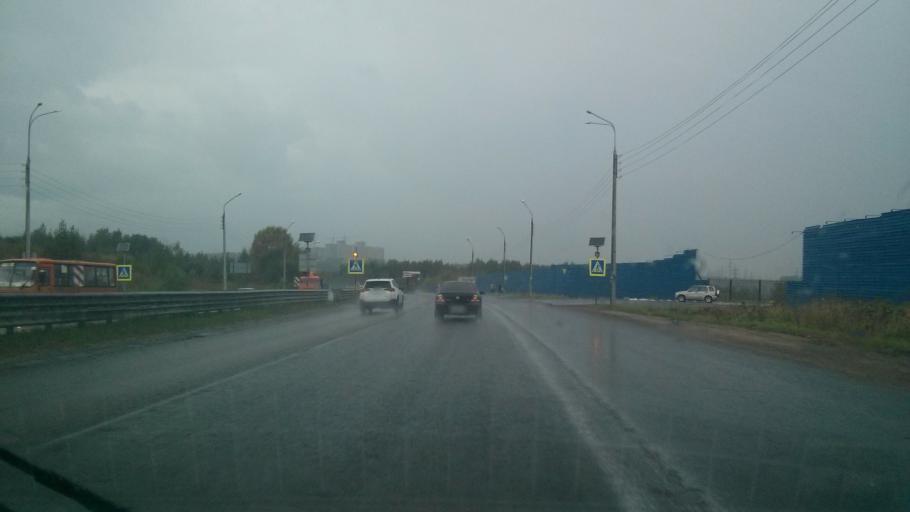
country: RU
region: Nizjnij Novgorod
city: Afonino
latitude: 56.2286
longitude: 44.0740
